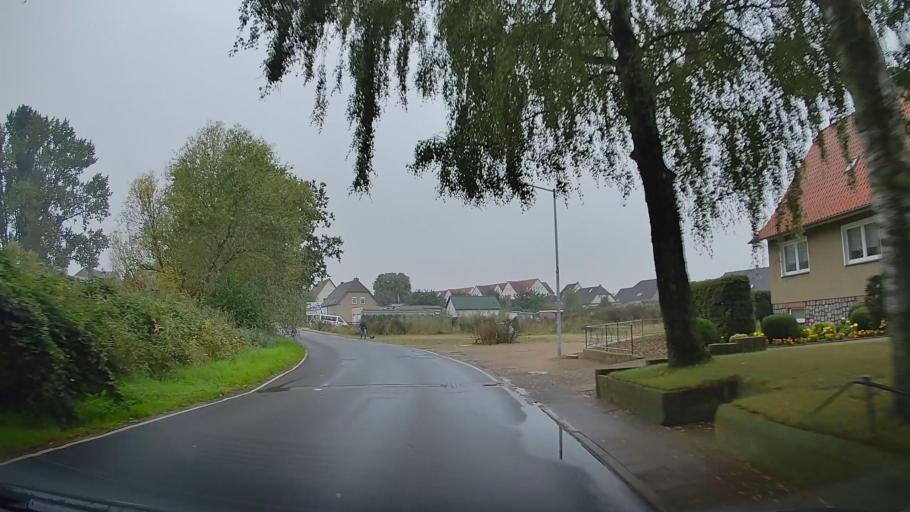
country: DE
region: Mecklenburg-Vorpommern
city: Wismar
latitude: 53.9058
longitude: 11.4053
